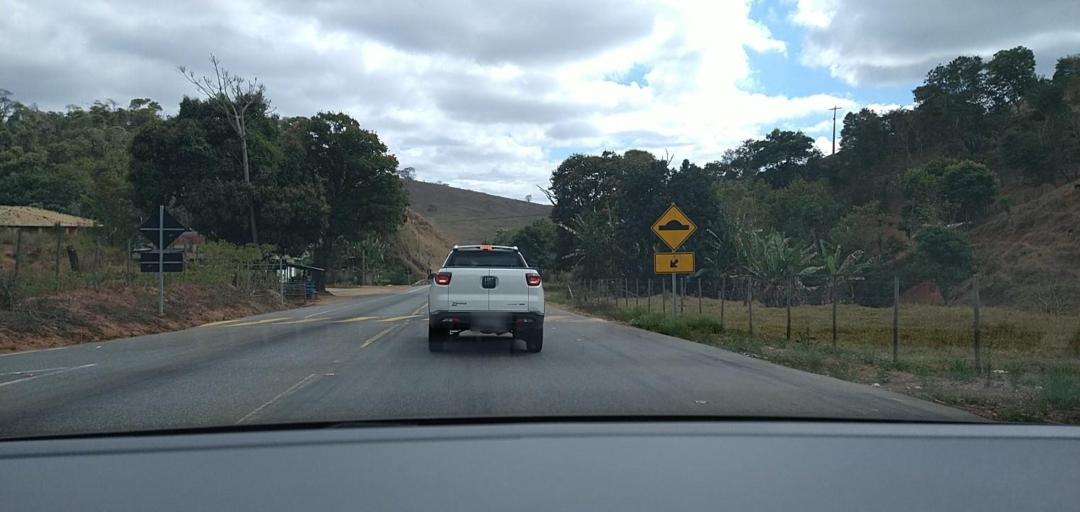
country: BR
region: Minas Gerais
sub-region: Ponte Nova
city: Ponte Nova
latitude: -20.5183
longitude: -42.8965
